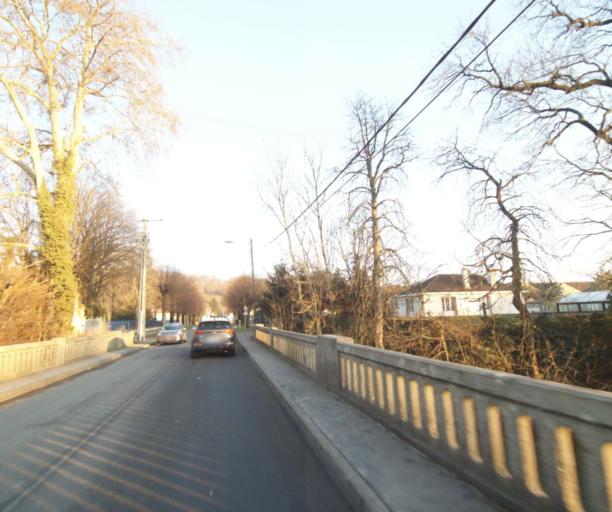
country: FR
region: Champagne-Ardenne
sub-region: Departement de la Haute-Marne
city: Bienville
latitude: 48.5836
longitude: 5.0428
